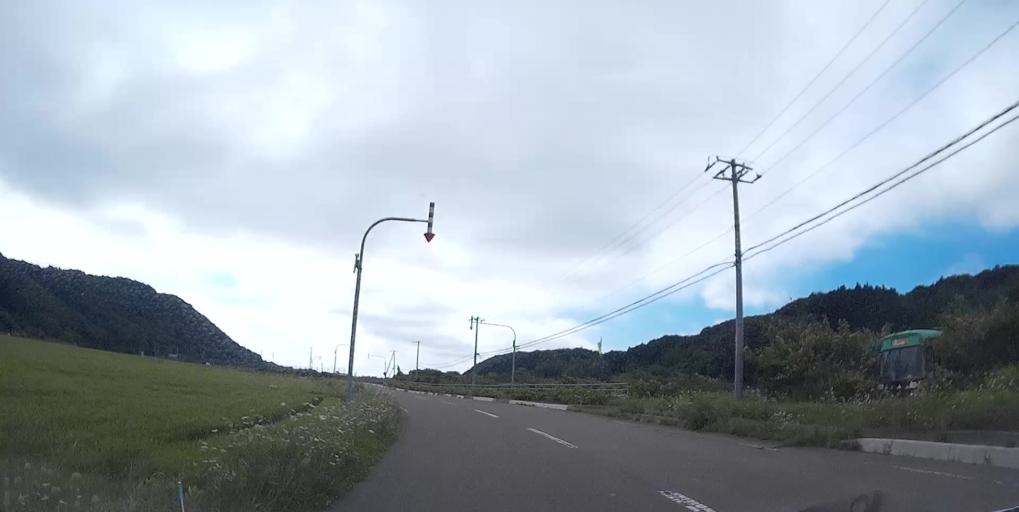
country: JP
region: Hokkaido
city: Kamiiso
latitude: 41.9738
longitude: 140.1601
